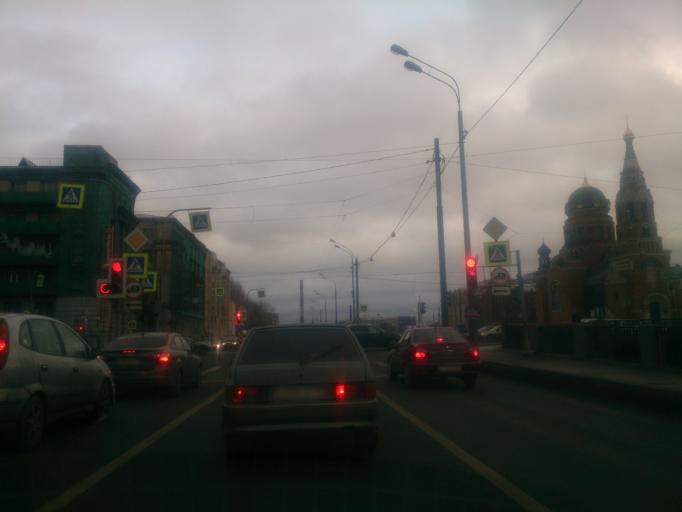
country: RU
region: St.-Petersburg
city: Admiralteisky
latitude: 59.9090
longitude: 30.3063
